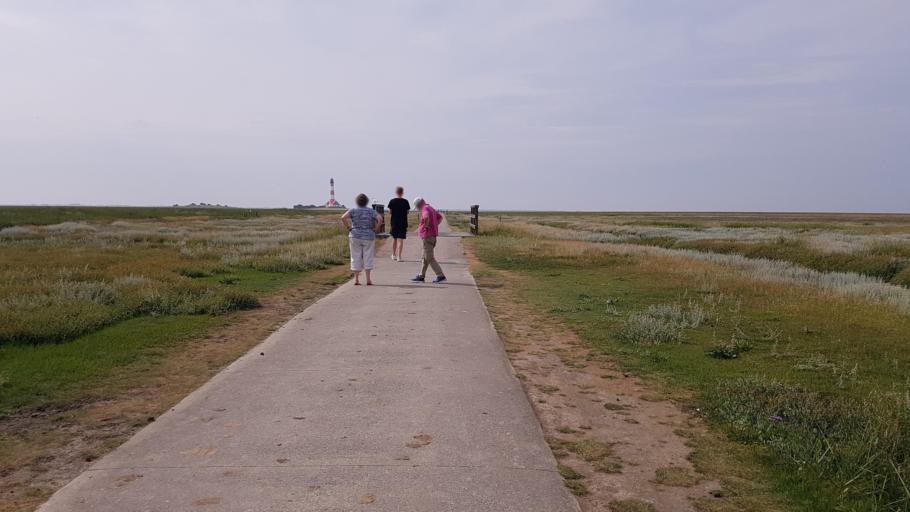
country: DE
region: Schleswig-Holstein
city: Westerhever
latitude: 54.3820
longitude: 8.6412
